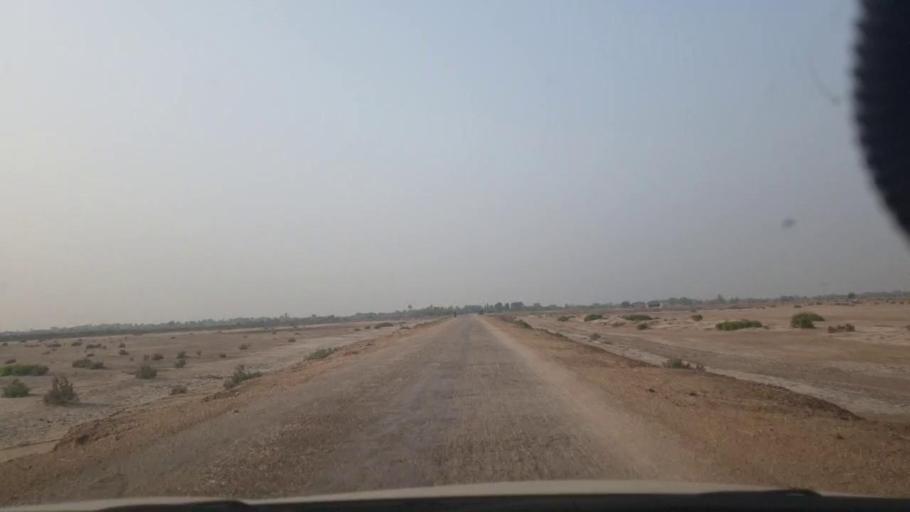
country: PK
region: Sindh
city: Bulri
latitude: 24.8181
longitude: 68.4053
